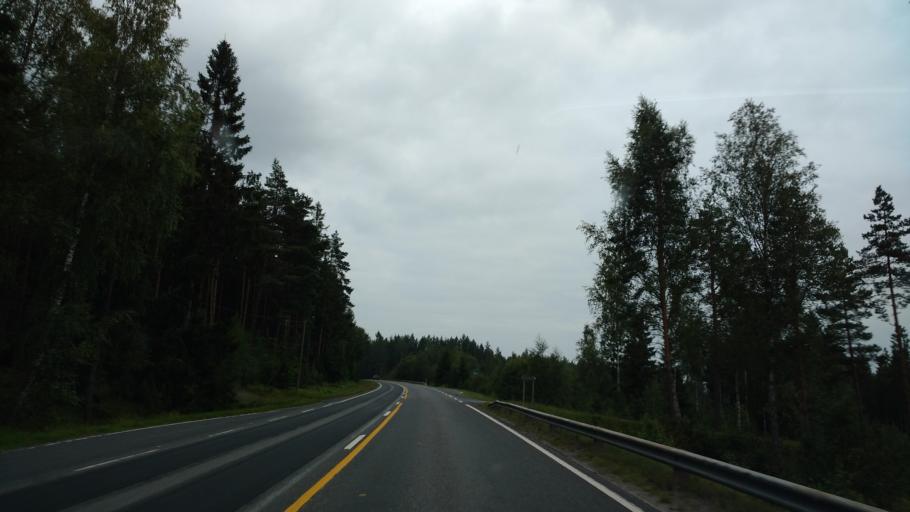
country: FI
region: Varsinais-Suomi
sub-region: Salo
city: Halikko
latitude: 60.4548
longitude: 23.0251
